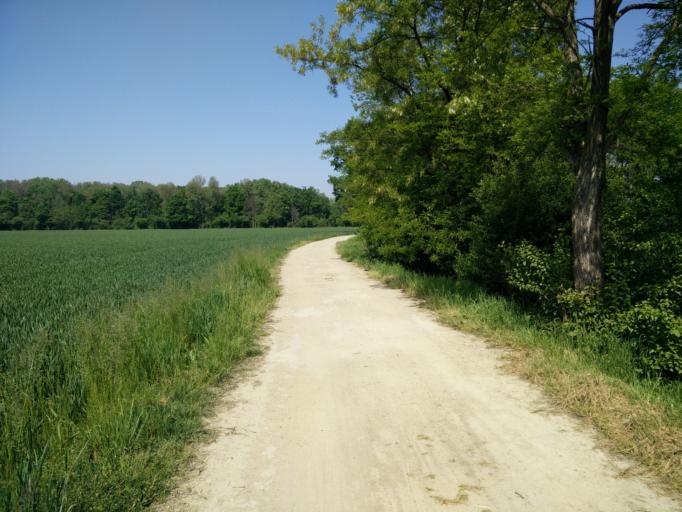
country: IT
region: Piedmont
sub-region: Provincia di Torino
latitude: 44.9587
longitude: 7.5635
